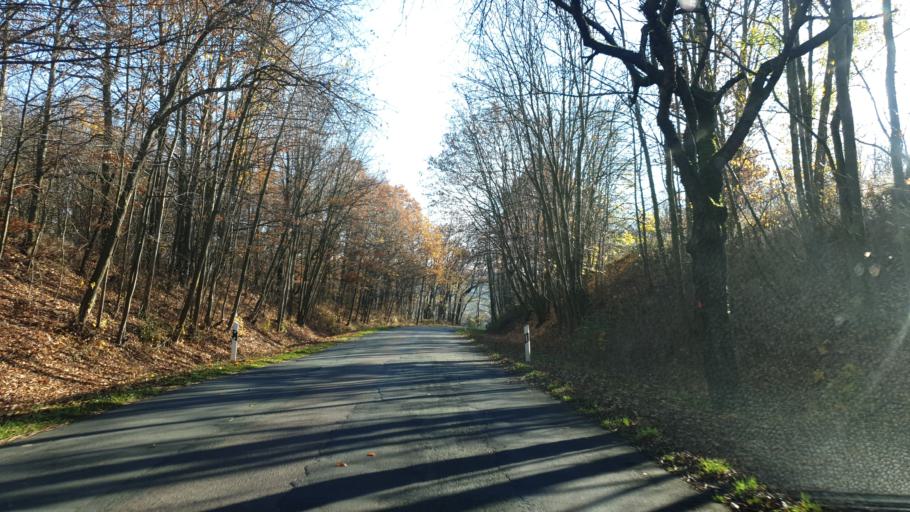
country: DE
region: Saxony-Anhalt
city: Wetterzeube
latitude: 51.0126
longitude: 12.0040
